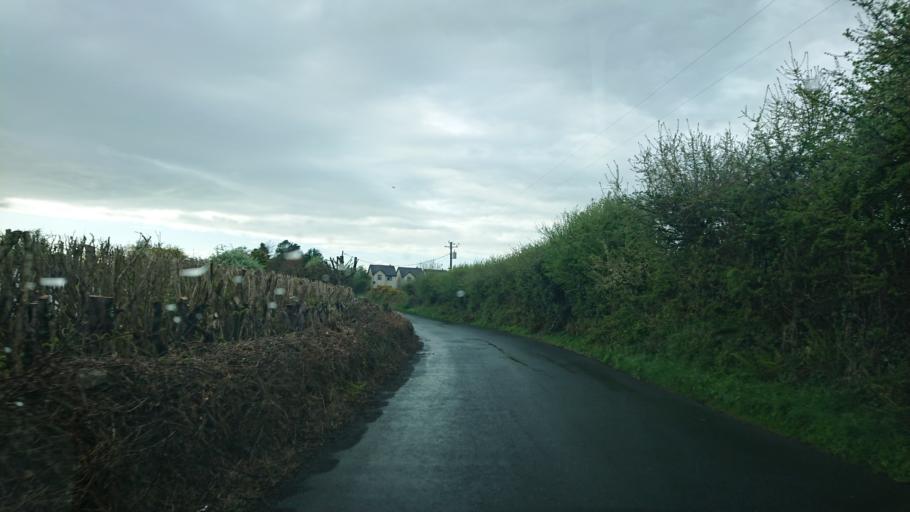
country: IE
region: Munster
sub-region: Waterford
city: Waterford
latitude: 52.2323
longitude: -7.0754
